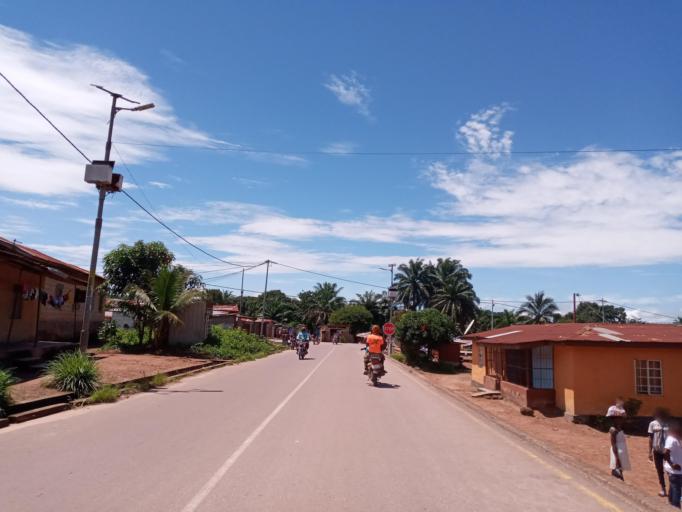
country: SL
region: Eastern Province
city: Koidu
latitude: 8.6467
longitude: -10.9650
